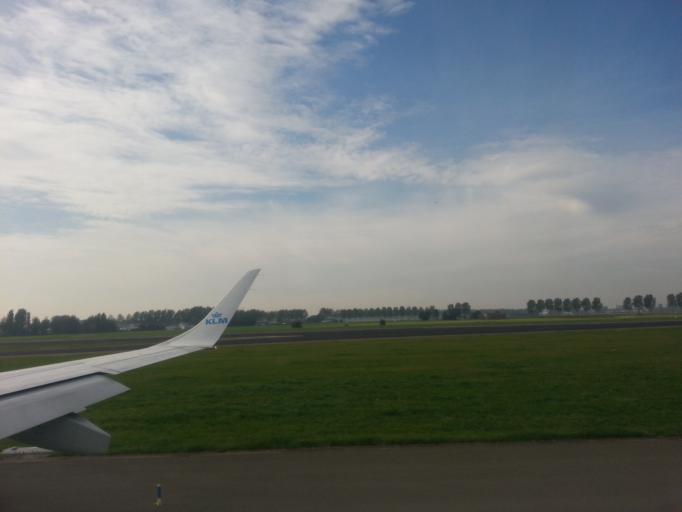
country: NL
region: North Holland
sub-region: Gemeente Haarlemmermeer
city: Hoofddorp
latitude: 52.3380
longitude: 4.7125
